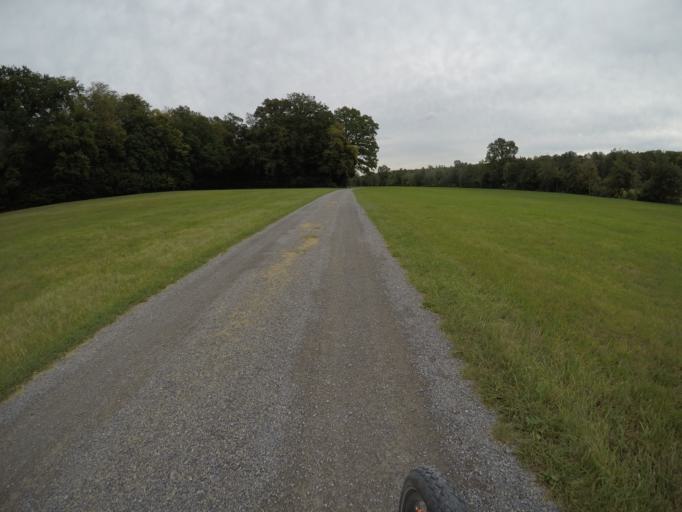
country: DE
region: Baden-Wuerttemberg
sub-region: Karlsruhe Region
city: Muhlacker
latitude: 48.9708
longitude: 8.8767
